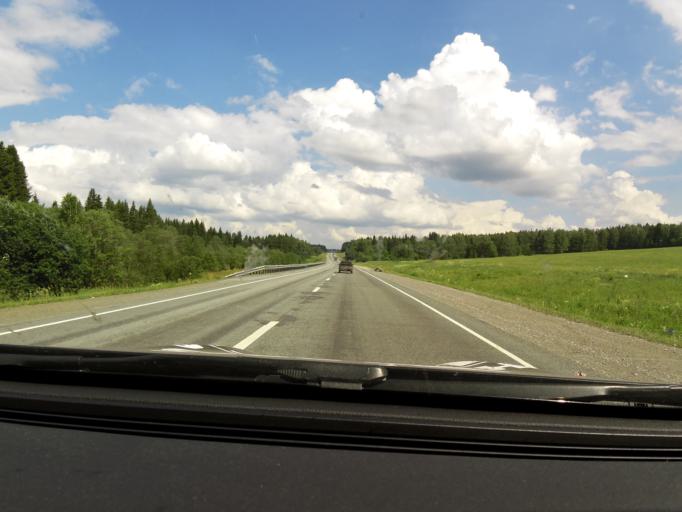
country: RU
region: Sverdlovsk
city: Arti
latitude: 56.7963
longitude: 58.6522
